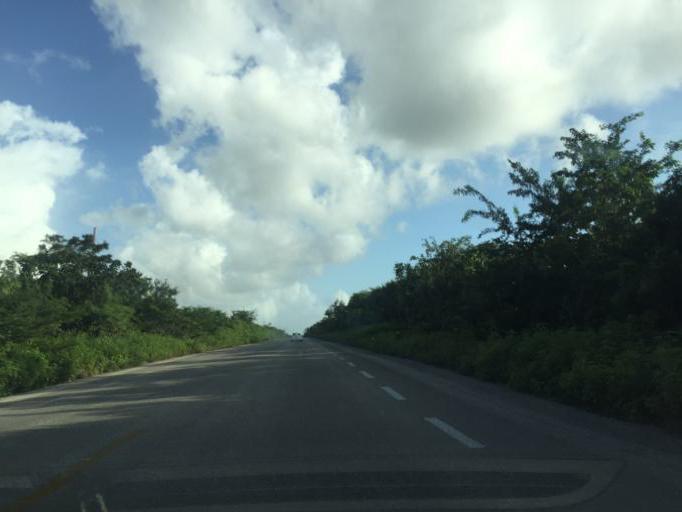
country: MX
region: Quintana Roo
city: Coba
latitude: 20.4656
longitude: -87.6825
